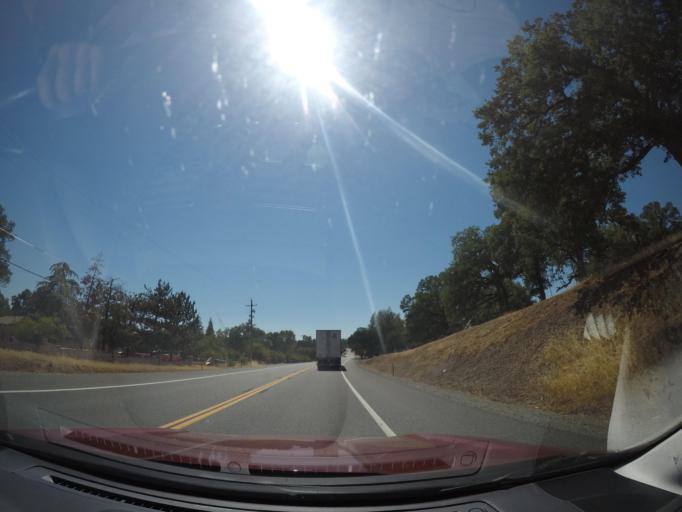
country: US
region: California
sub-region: Shasta County
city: Bella Vista
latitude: 40.6395
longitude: -122.2351
